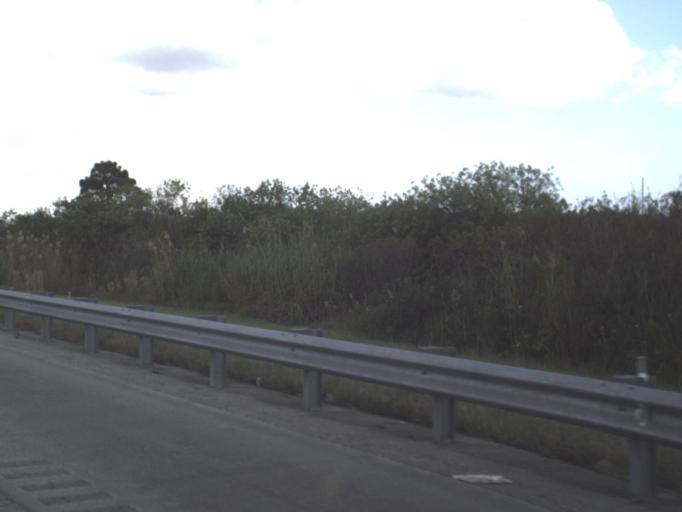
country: US
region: Florida
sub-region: Palm Beach County
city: Tequesta
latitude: 27.0066
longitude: -80.2098
